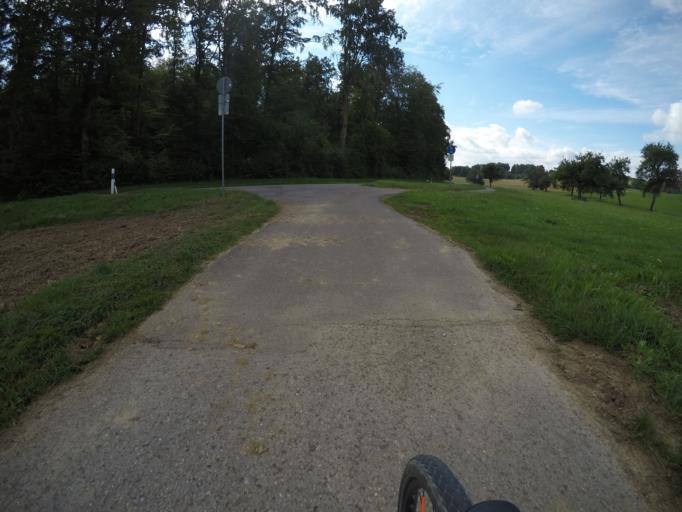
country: DE
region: Baden-Wuerttemberg
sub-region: Karlsruhe Region
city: Gechingen
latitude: 48.7075
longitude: 8.8155
